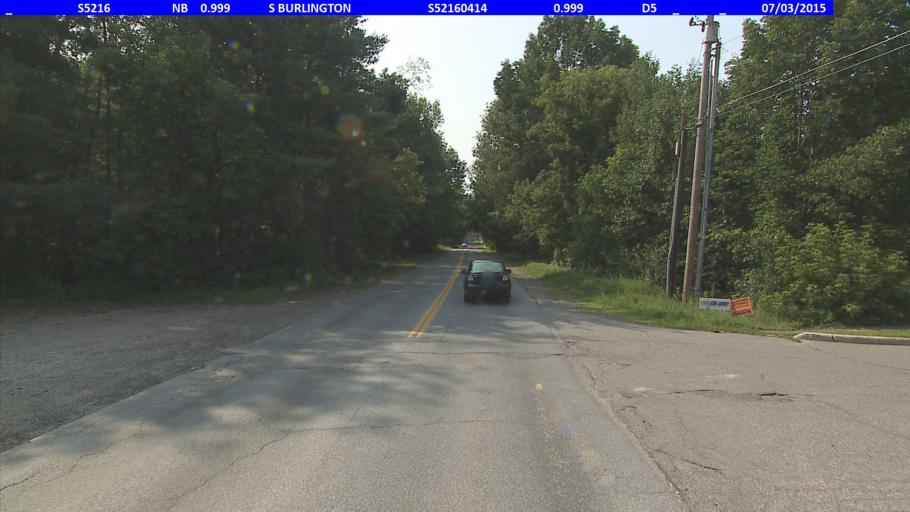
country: US
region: Vermont
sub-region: Chittenden County
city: Winooski
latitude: 44.4798
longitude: -73.1782
